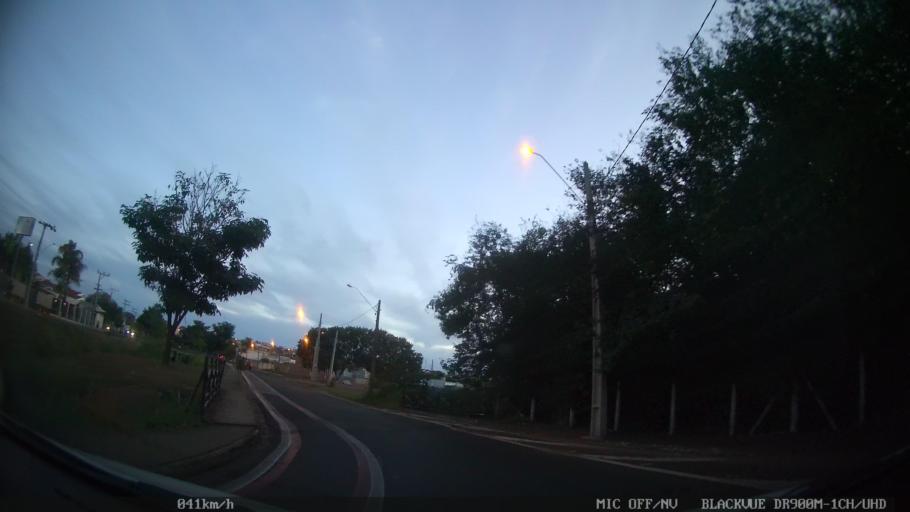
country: BR
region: Sao Paulo
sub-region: Catanduva
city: Catanduva
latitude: -21.1342
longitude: -48.9892
